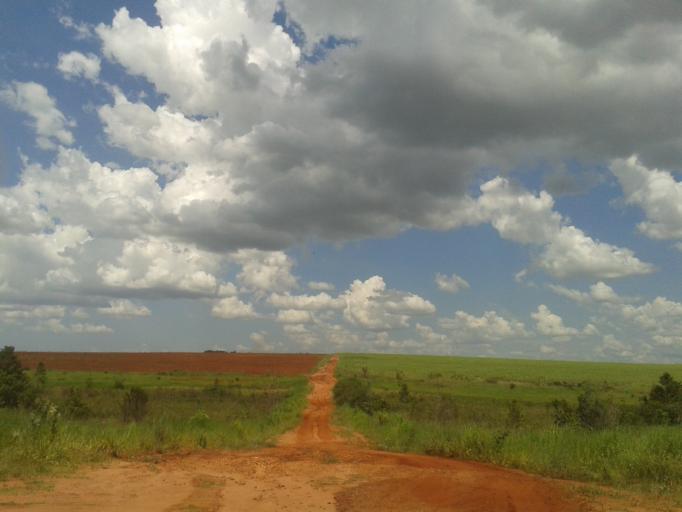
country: BR
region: Minas Gerais
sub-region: Santa Vitoria
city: Santa Vitoria
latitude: -19.1742
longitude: -50.4366
